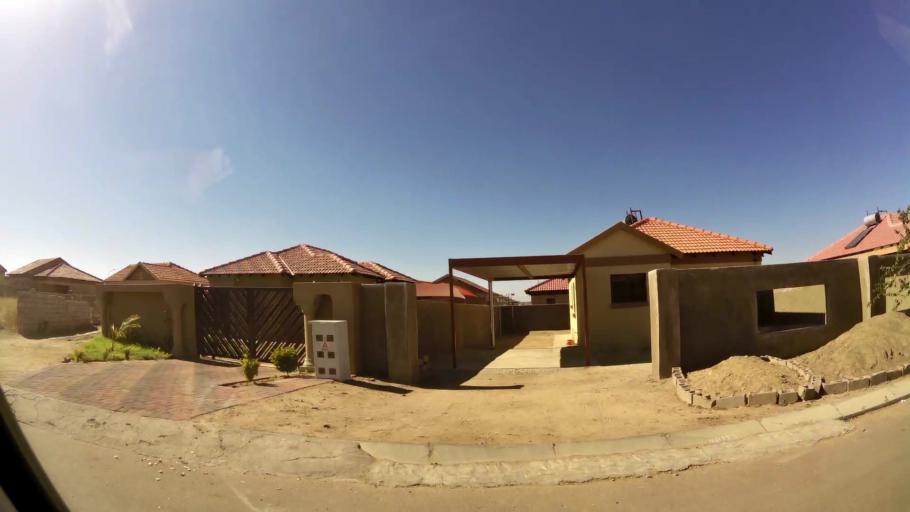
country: ZA
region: Limpopo
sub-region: Capricorn District Municipality
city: Polokwane
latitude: -23.8583
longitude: 29.4243
